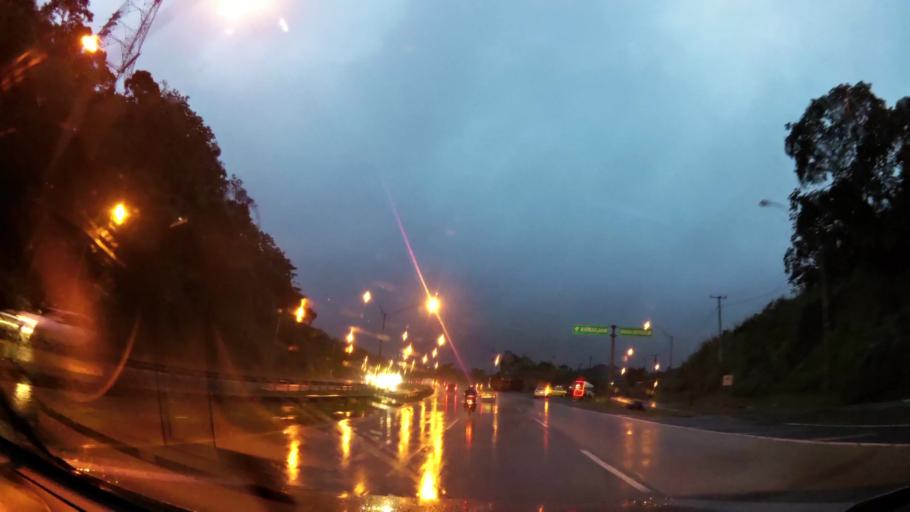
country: PA
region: Panama
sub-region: Distrito de Panama
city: Paraiso
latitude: 9.0267
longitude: -79.6388
